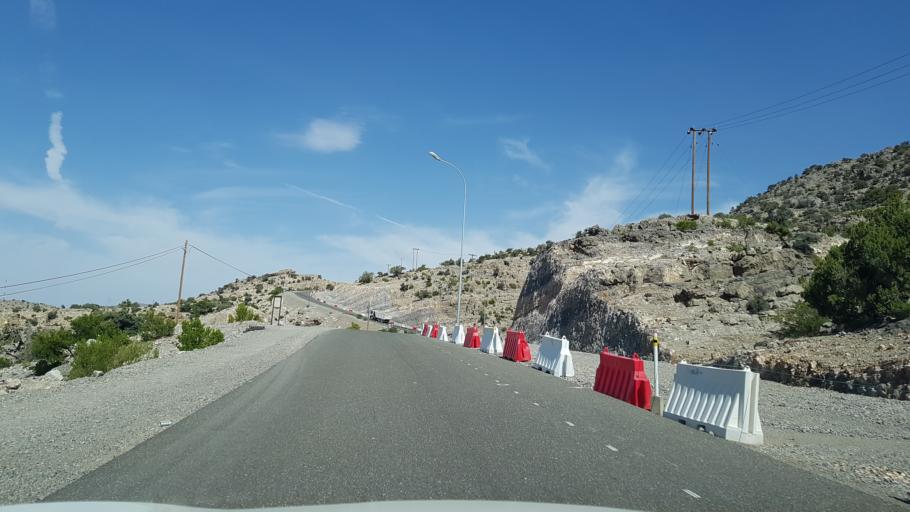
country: OM
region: Muhafazat ad Dakhiliyah
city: Nizwa
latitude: 23.1136
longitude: 57.6485
